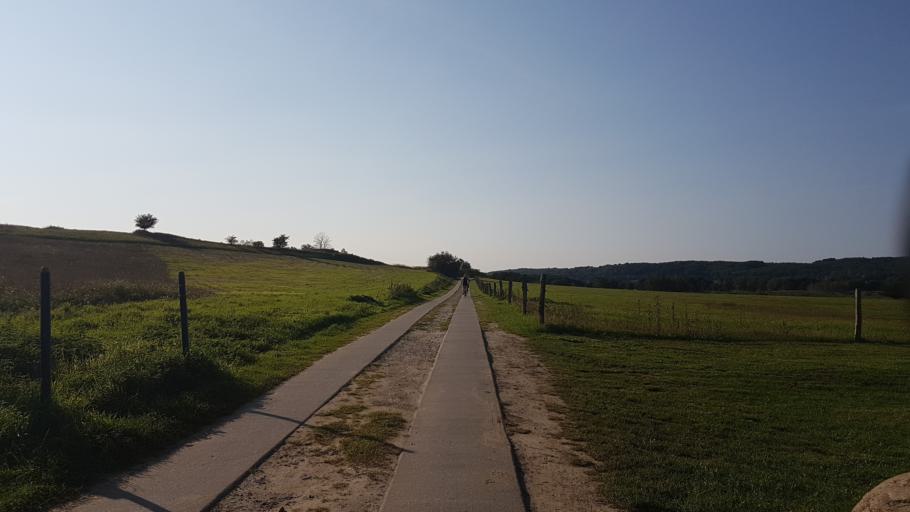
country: DE
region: Mecklenburg-Vorpommern
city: Ostseebad Sellin
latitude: 54.3557
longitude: 13.6489
